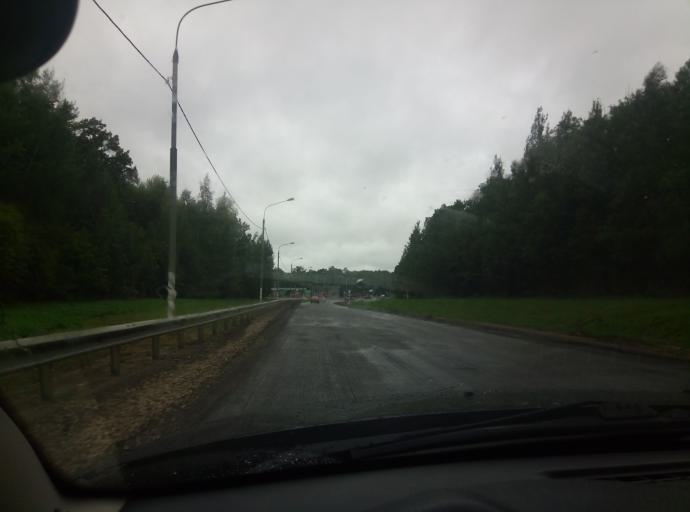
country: RU
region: Tula
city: Leninskiy
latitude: 54.4113
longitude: 37.5016
